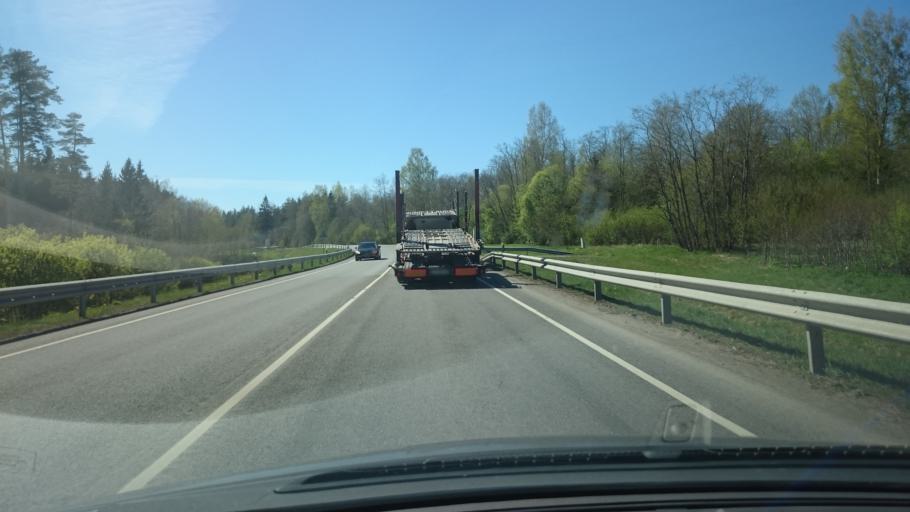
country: EE
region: Ida-Virumaa
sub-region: Toila vald
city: Voka
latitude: 59.3805
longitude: 27.5548
